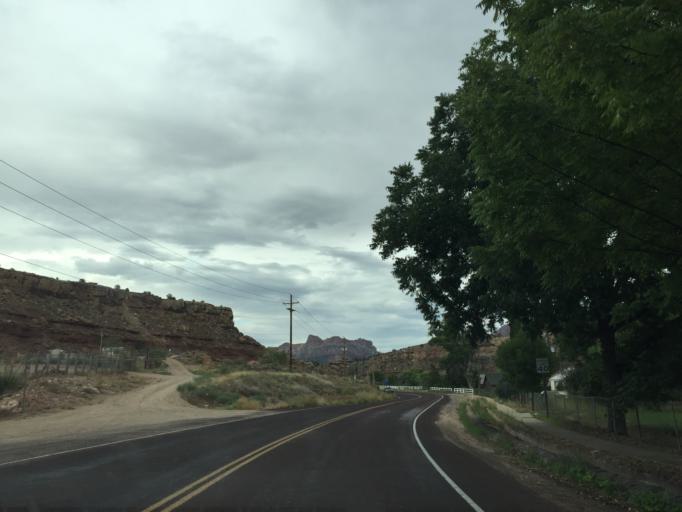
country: US
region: Utah
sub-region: Washington County
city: Hildale
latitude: 37.1613
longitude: -113.0354
